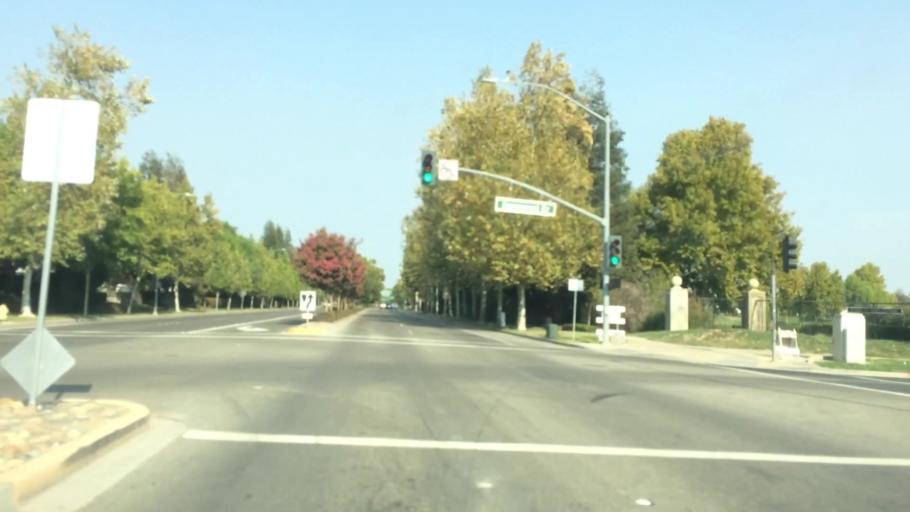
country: US
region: California
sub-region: Contra Costa County
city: Brentwood
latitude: 37.9253
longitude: -121.7295
